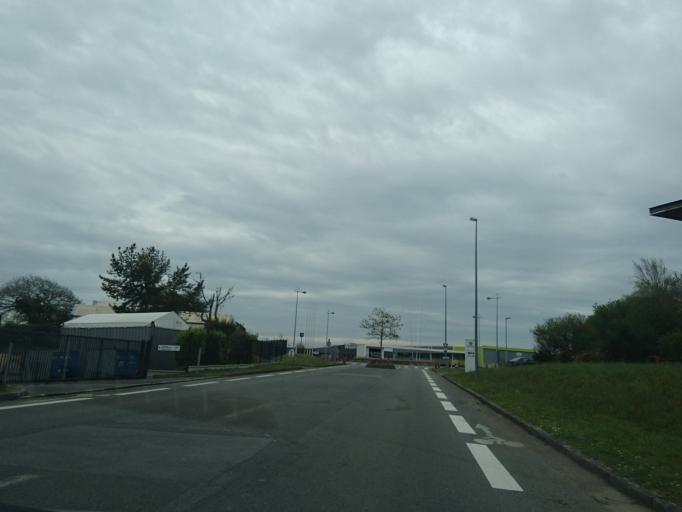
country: FR
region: Brittany
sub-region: Departement du Finistere
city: Roscanvel
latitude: 48.3611
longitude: -4.5704
